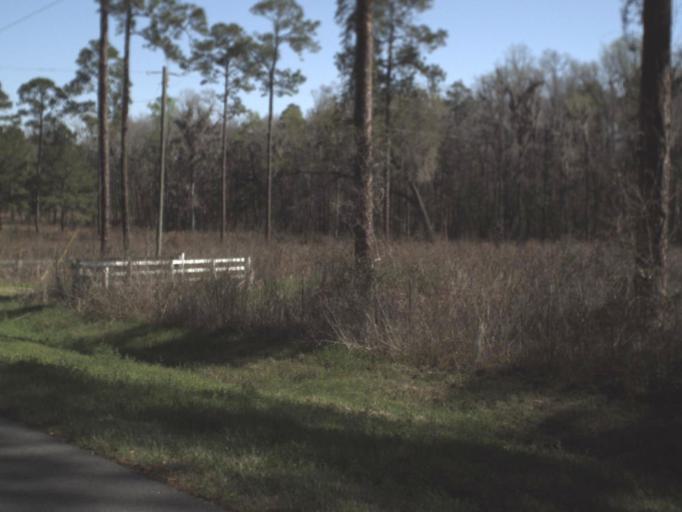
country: US
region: Florida
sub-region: Jefferson County
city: Monticello
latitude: 30.4078
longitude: -84.0209
